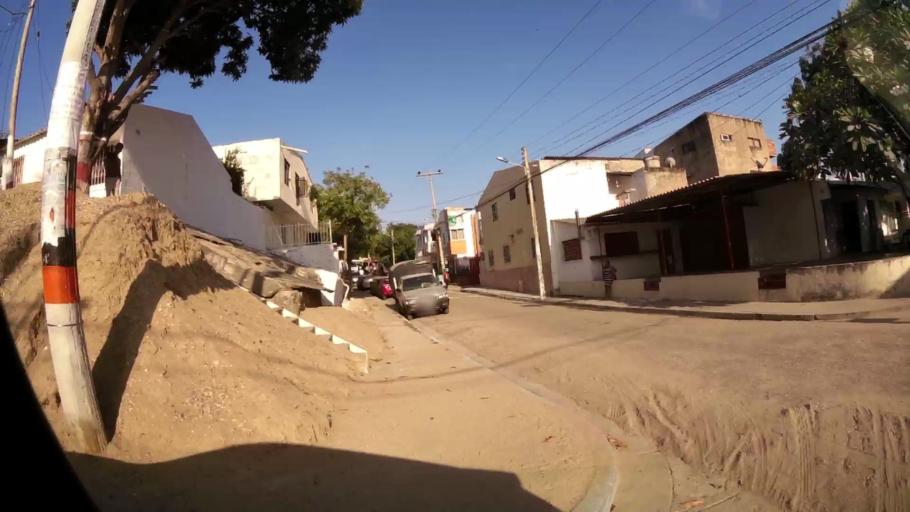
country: CO
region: Bolivar
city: Cartagena
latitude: 10.4022
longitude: -75.4836
